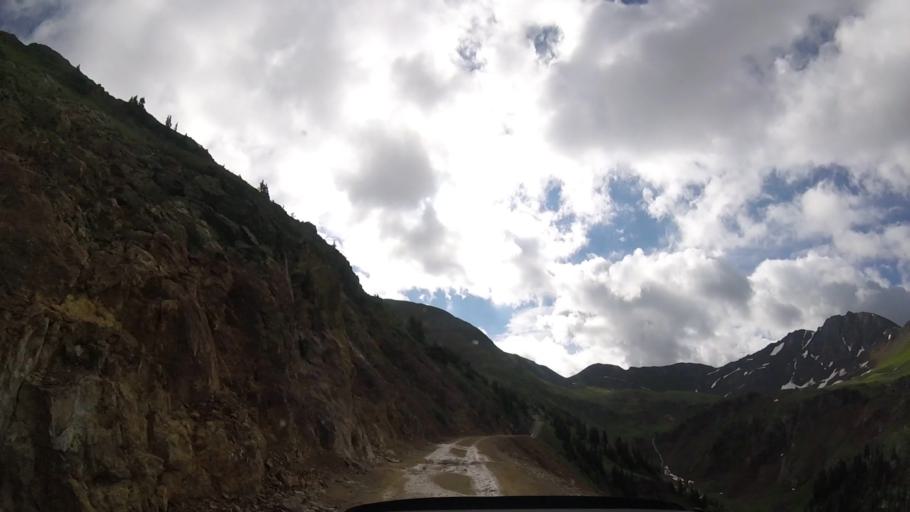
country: US
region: Colorado
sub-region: San Juan County
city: Silverton
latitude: 37.9134
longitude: -107.6363
